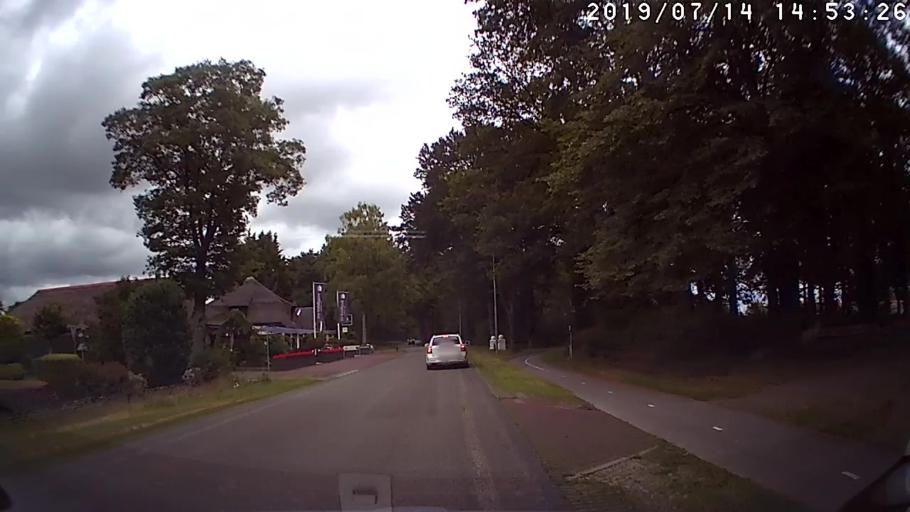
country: NL
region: Overijssel
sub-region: Gemeente Raalte
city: Heino
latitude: 52.4371
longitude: 6.2611
